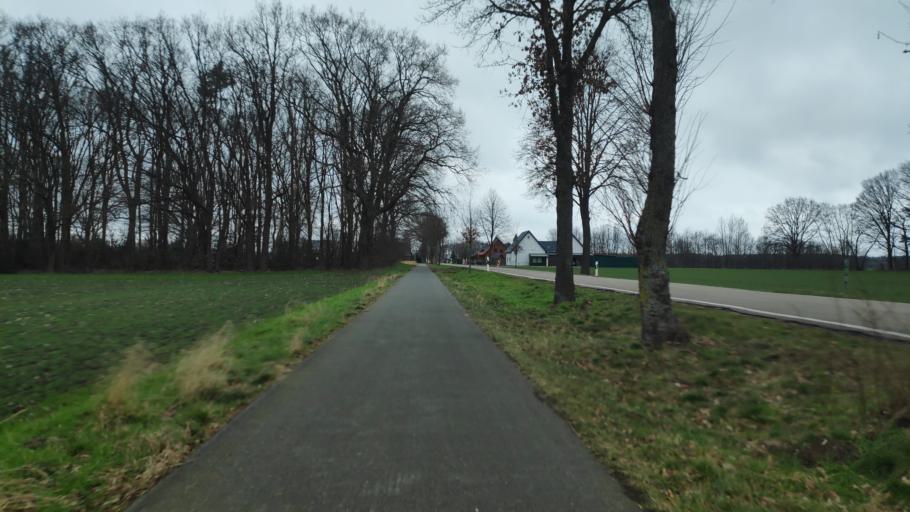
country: DE
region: North Rhine-Westphalia
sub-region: Regierungsbezirk Detmold
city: Hille
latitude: 52.3548
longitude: 8.7852
